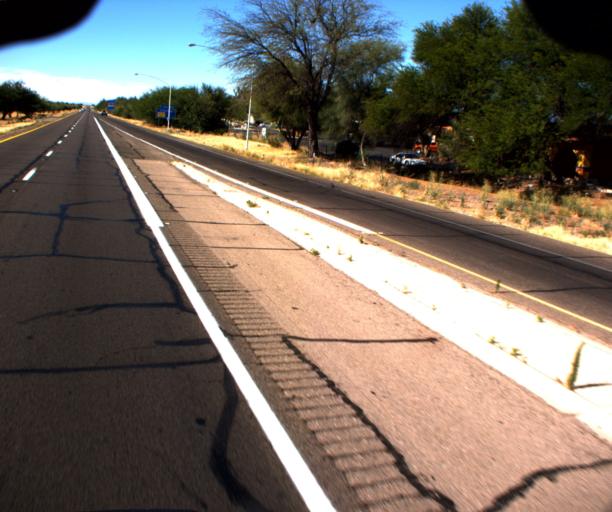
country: US
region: Arizona
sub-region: Pima County
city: Green Valley
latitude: 31.8685
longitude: -110.9910
